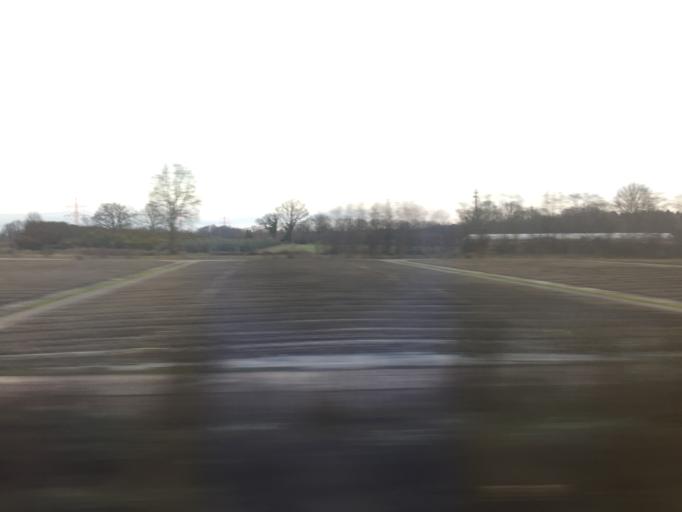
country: DE
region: Schleswig-Holstein
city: Prisdorf
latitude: 53.6823
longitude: 9.7441
